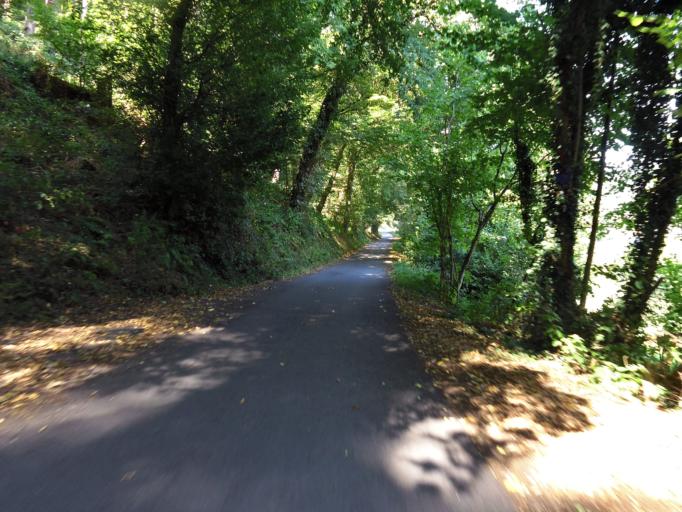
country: DE
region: Baden-Wuerttemberg
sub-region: Karlsruhe Region
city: Neunkirchen
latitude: 49.4207
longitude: 8.9998
